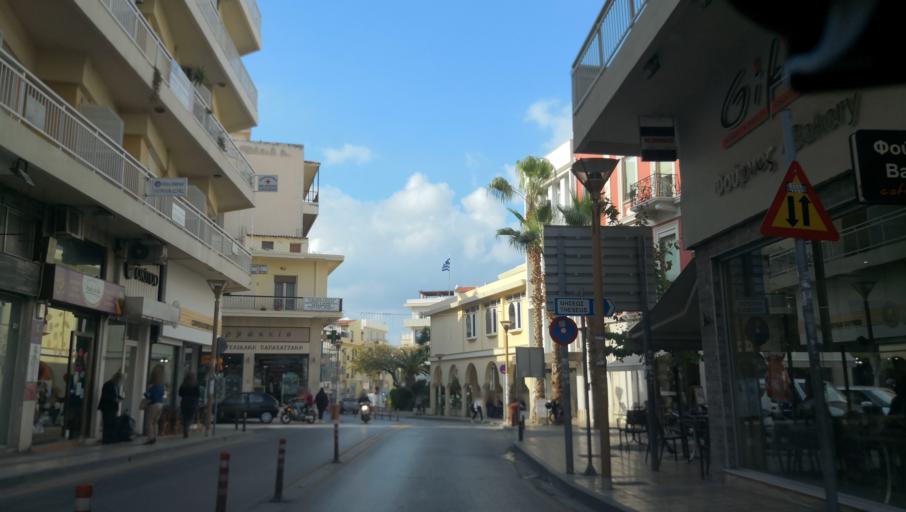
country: GR
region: Crete
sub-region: Nomos Irakleiou
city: Irakleion
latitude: 35.3368
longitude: 25.1313
